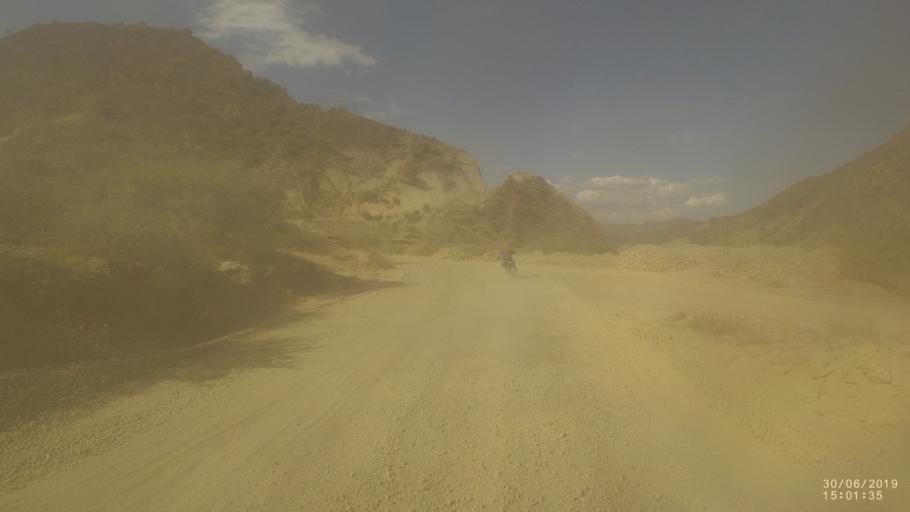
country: BO
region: Cochabamba
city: Irpa Irpa
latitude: -17.7330
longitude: -66.3356
